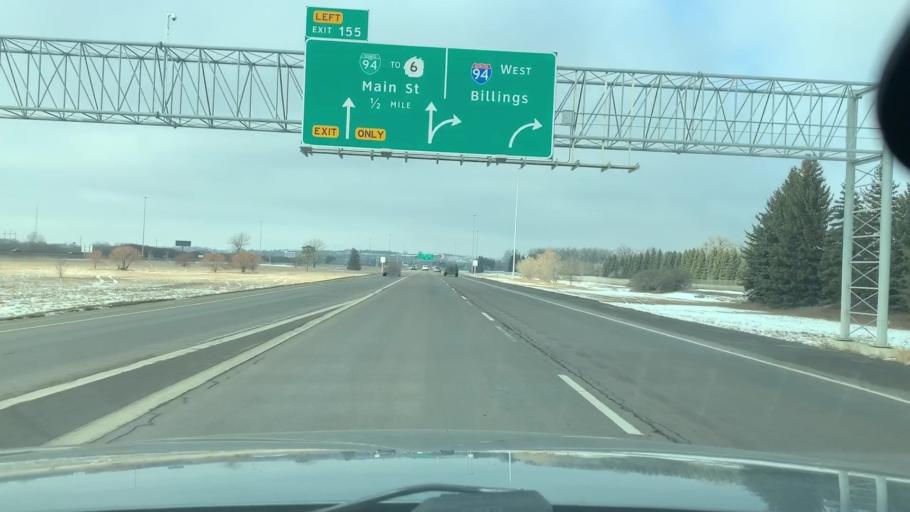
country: US
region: North Dakota
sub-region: Morton County
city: Mandan
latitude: 46.8232
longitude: -100.8442
